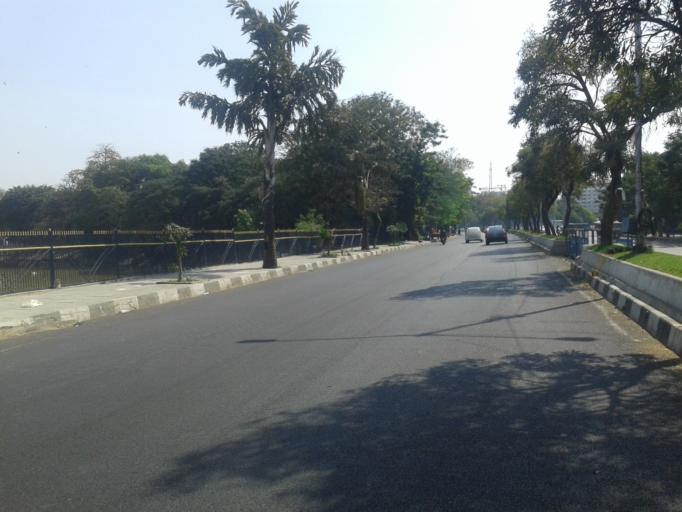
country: IN
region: Telangana
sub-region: Hyderabad
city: Hyderabad
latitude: 17.4117
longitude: 78.4713
